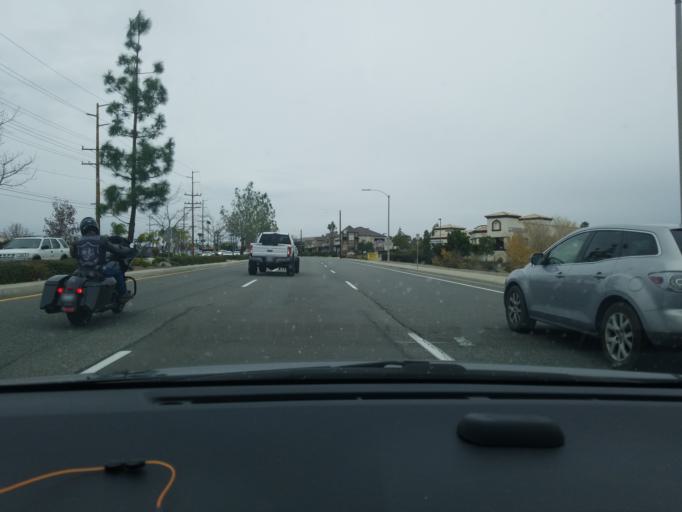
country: US
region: California
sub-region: Riverside County
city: Temecula
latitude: 33.5092
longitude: -117.1506
